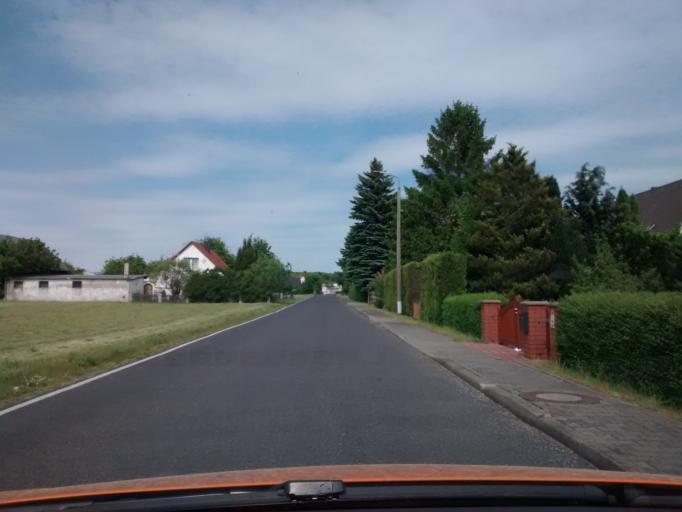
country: DE
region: Brandenburg
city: Ihlow
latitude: 51.9231
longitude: 13.3310
